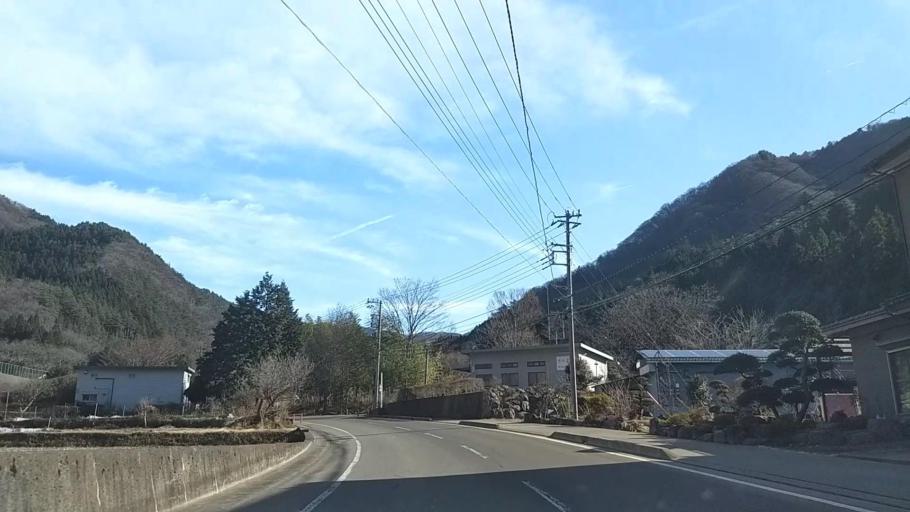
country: JP
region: Yamanashi
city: Otsuki
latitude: 35.5292
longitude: 138.9178
